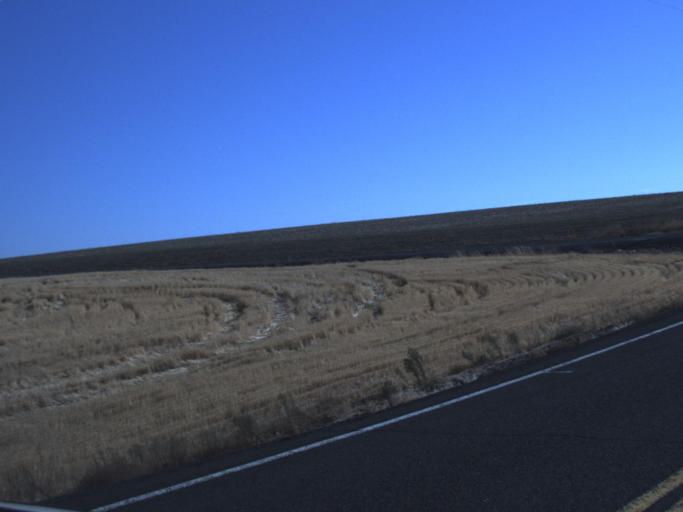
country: US
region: Washington
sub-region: Adams County
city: Ritzville
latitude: 46.8685
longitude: -118.5469
